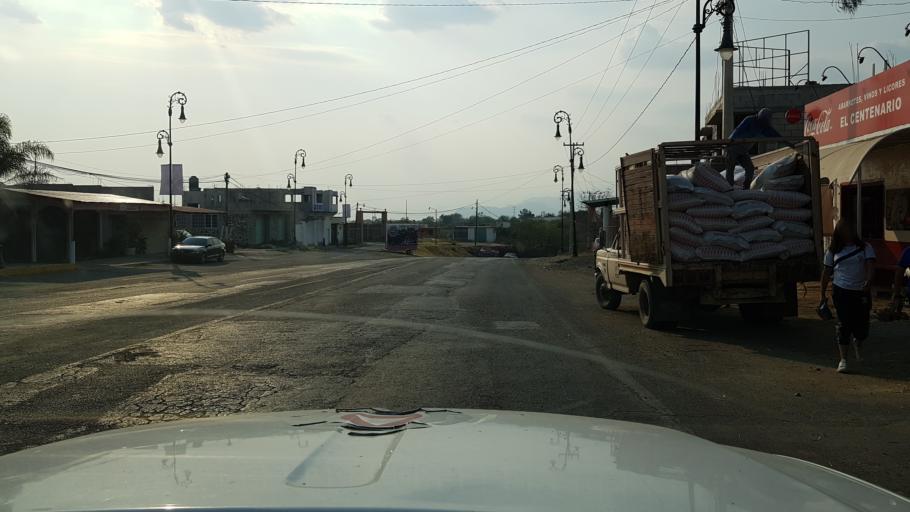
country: MX
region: Morelos
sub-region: Yecapixtla
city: Yecapixtla
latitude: 18.8866
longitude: -98.8732
